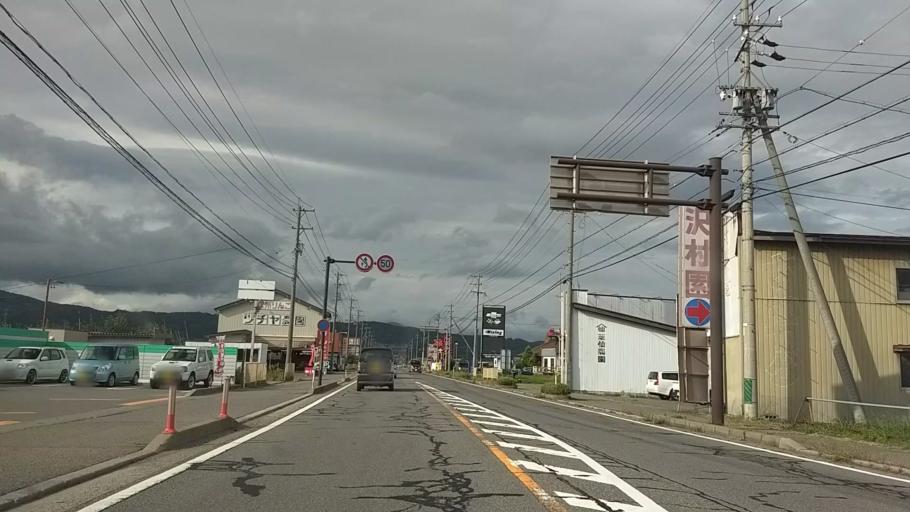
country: JP
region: Nagano
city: Suzaka
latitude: 36.6837
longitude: 138.2679
